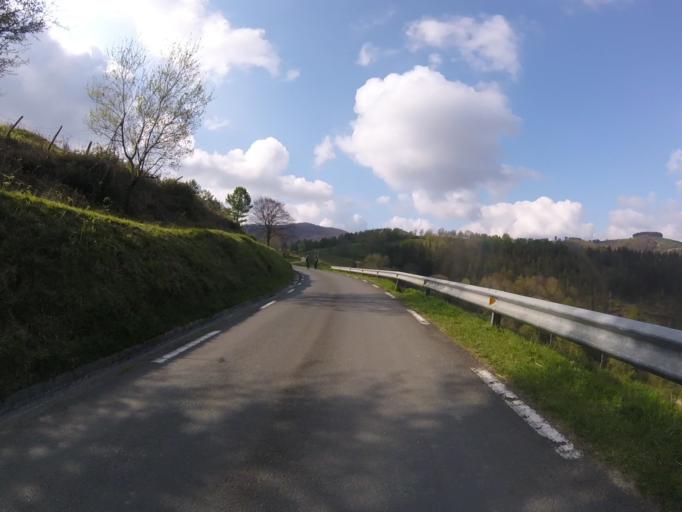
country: ES
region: Basque Country
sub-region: Provincia de Guipuzcoa
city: Azkoitia
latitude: 43.2205
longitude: -2.3105
